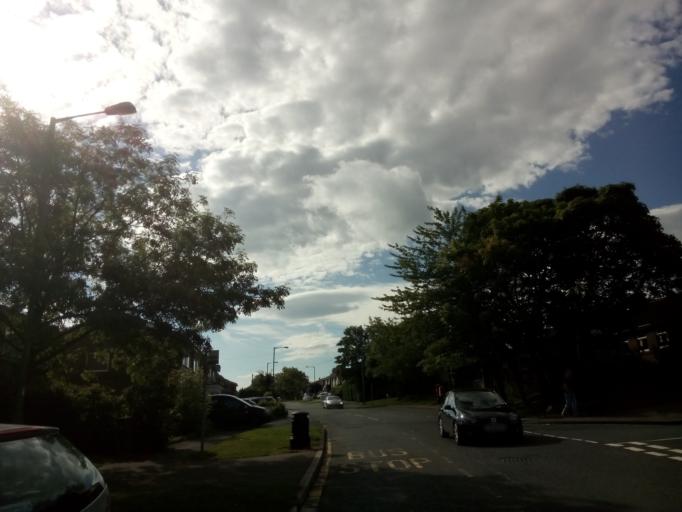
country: GB
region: England
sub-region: County Durham
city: Durham
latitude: 54.8040
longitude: -1.5670
